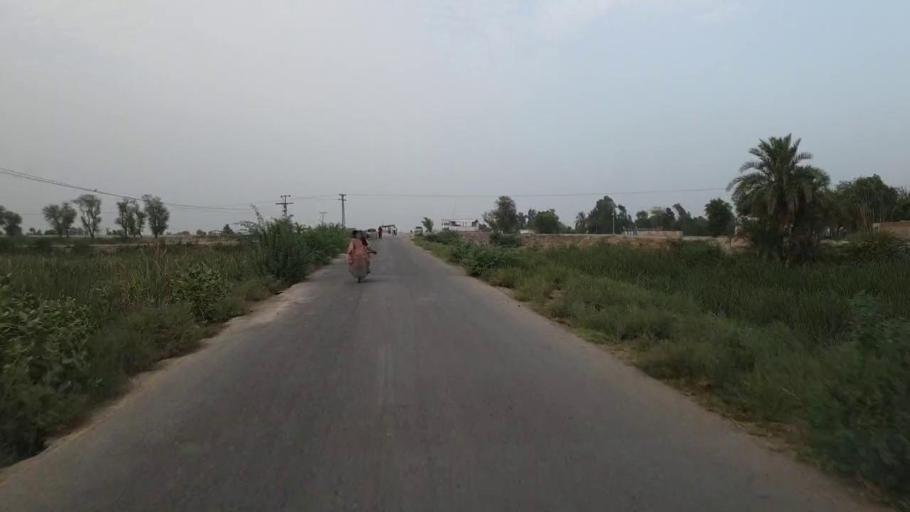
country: PK
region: Sindh
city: Daur
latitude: 26.4560
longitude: 68.2943
